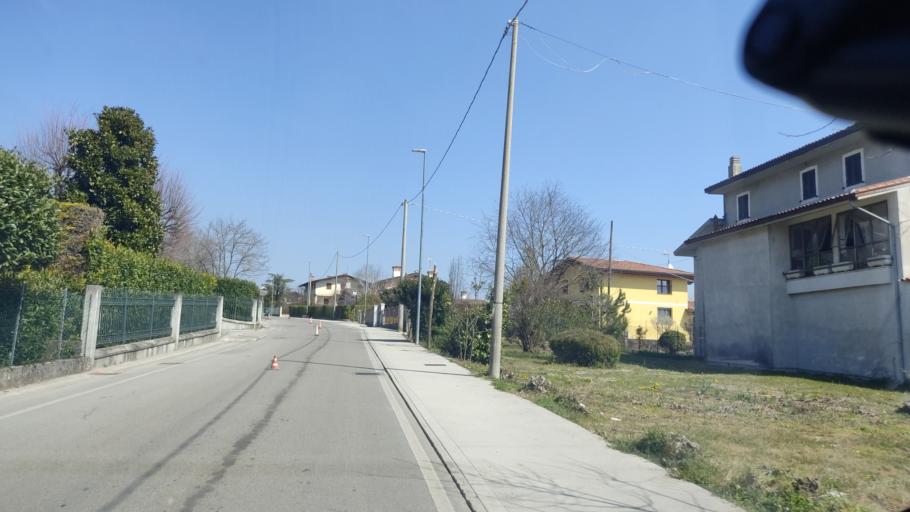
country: IT
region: Friuli Venezia Giulia
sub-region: Provincia di Pordenone
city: Budoia
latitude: 46.0348
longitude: 12.5338
